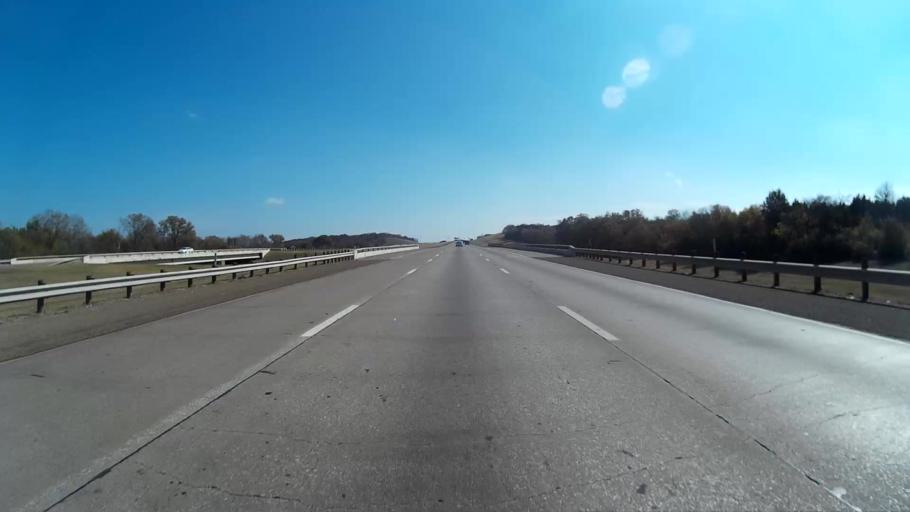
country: US
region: Texas
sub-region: Dallas County
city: Hutchins
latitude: 32.6747
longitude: -96.7385
